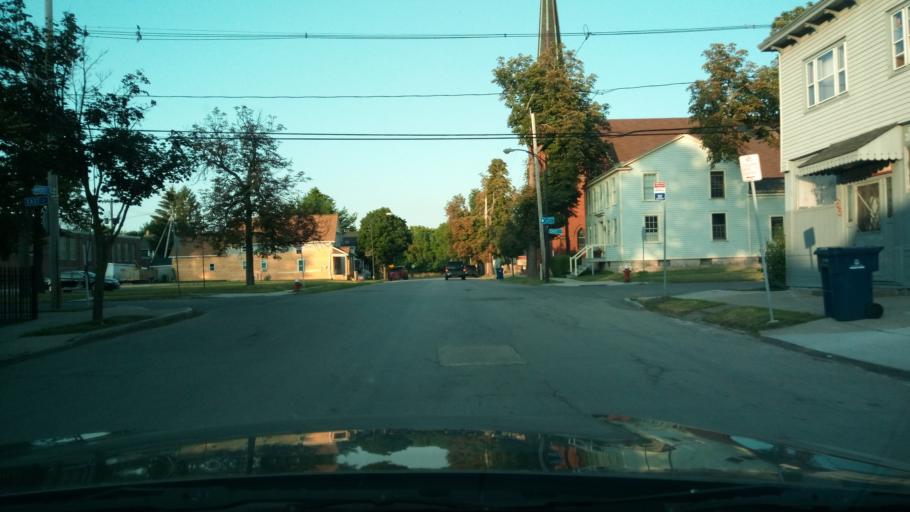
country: US
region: New York
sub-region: Erie County
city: Kenmore
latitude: 42.9349
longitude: -78.9007
